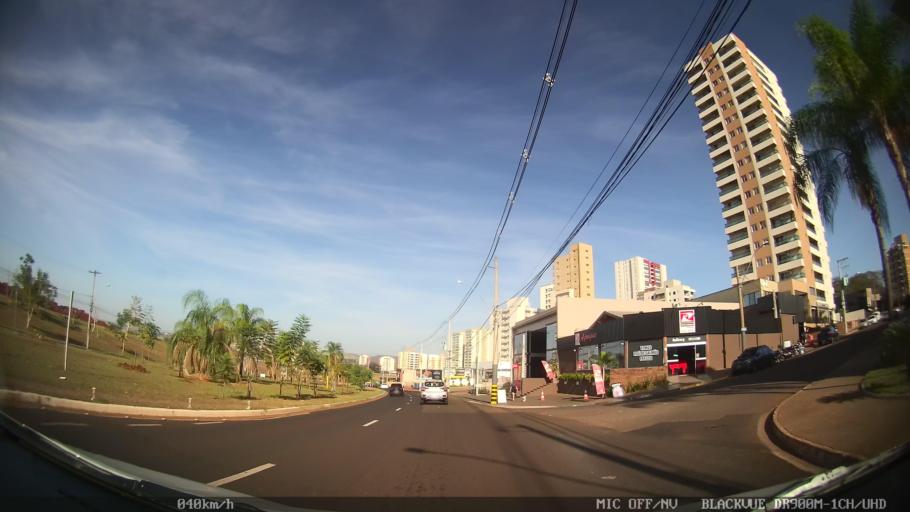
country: BR
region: Sao Paulo
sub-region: Ribeirao Preto
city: Ribeirao Preto
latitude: -21.2175
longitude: -47.8260
